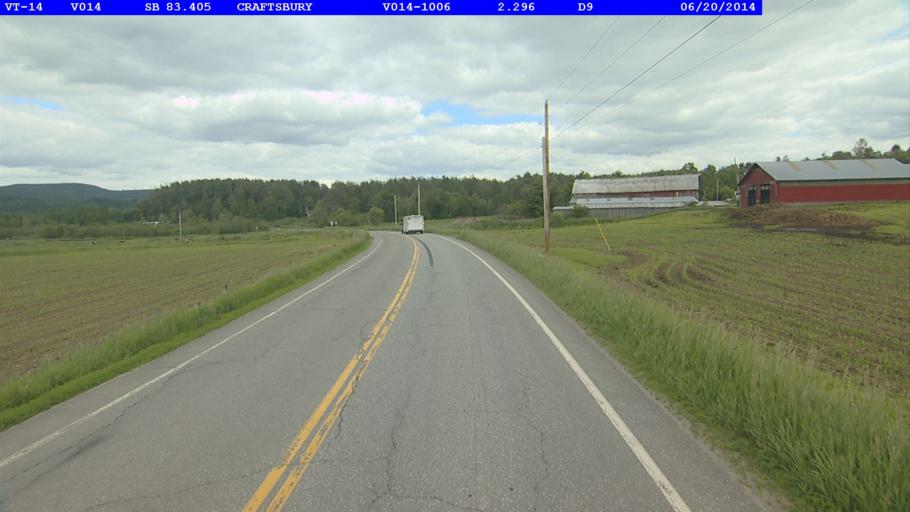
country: US
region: Vermont
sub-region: Caledonia County
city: Hardwick
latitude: 44.6271
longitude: -72.3883
